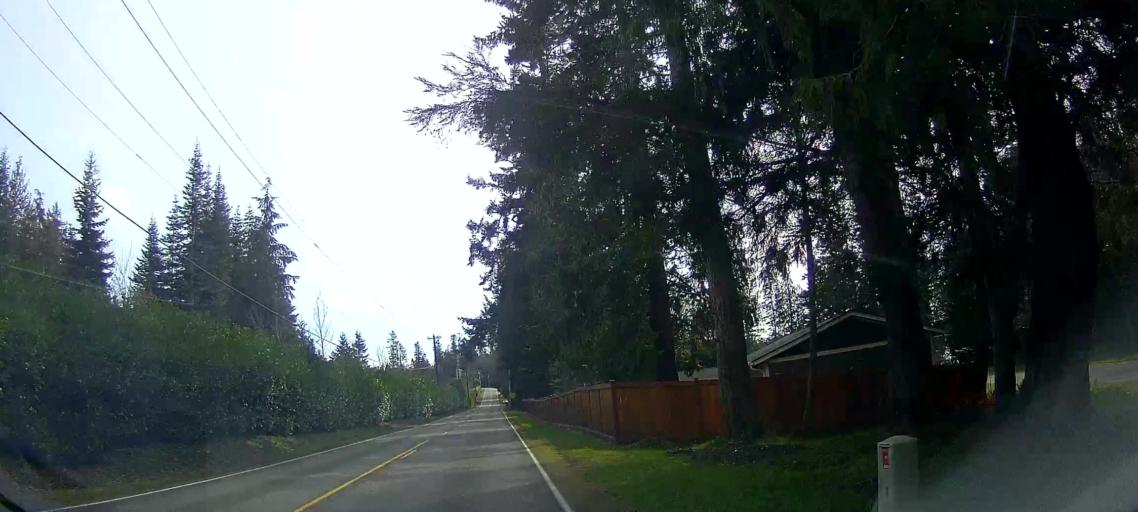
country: US
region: Washington
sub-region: Island County
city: Langley
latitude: 48.0978
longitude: -122.4142
